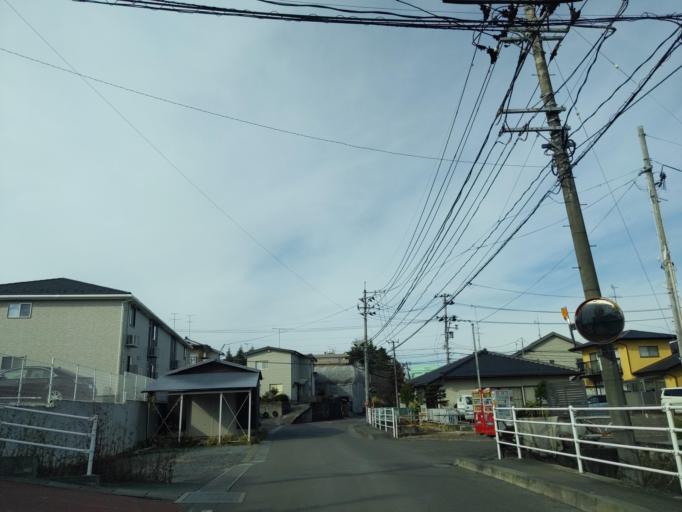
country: JP
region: Fukushima
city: Koriyama
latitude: 37.4161
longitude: 140.3781
